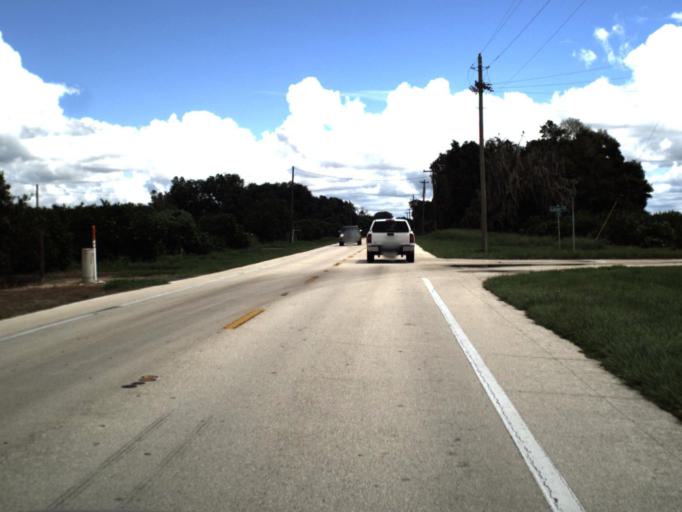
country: US
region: Florida
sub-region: Polk County
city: Fort Meade
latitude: 27.7481
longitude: -81.7488
